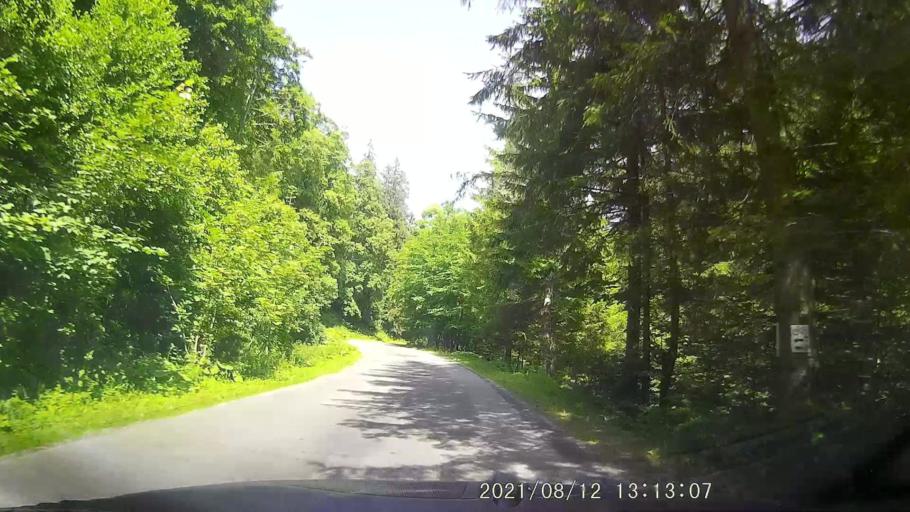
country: PL
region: Lower Silesian Voivodeship
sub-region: Powiat klodzki
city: Stronie Slaskie
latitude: 50.2515
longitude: 16.8522
